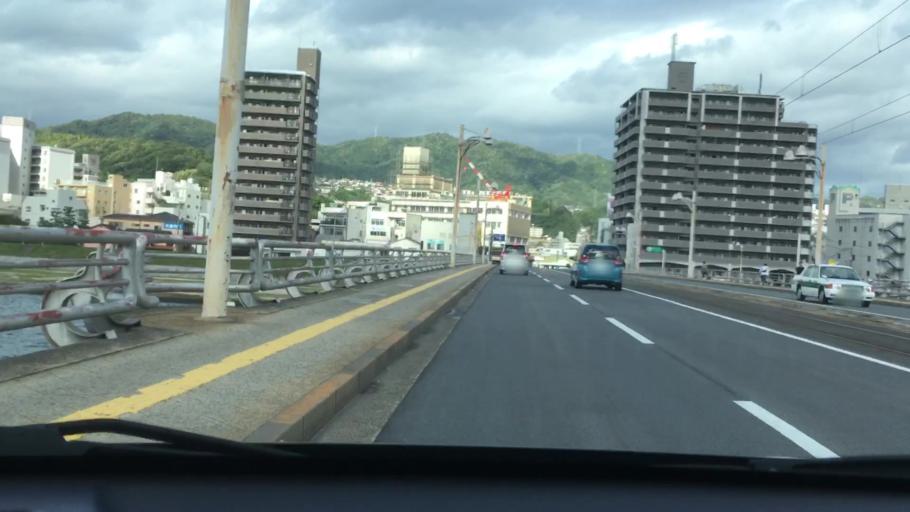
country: JP
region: Hiroshima
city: Hiroshima-shi
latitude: 34.3961
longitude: 132.4312
